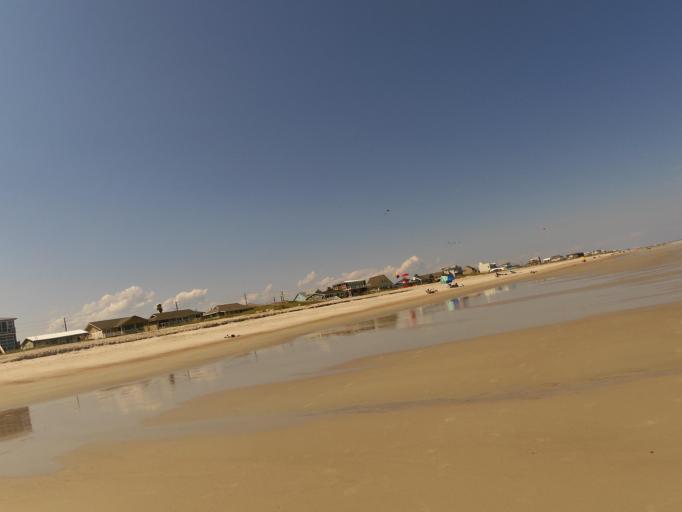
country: US
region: Florida
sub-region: Nassau County
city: Fernandina Beach
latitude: 30.6541
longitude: -81.4320
